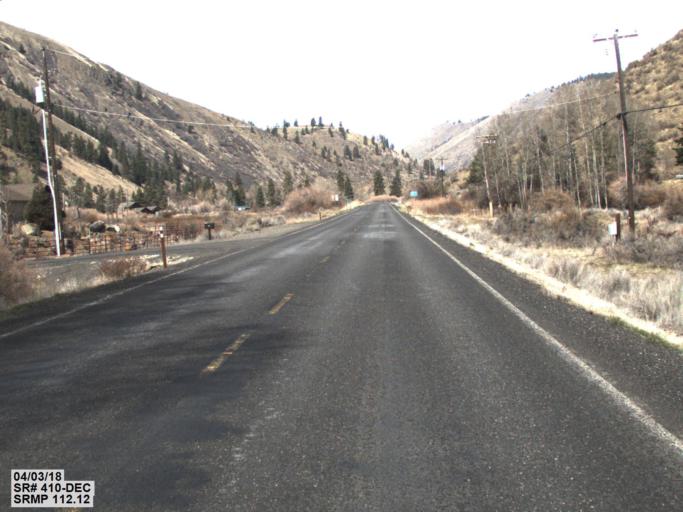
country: US
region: Washington
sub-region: Yakima County
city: Tieton
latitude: 46.7768
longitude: -120.8581
